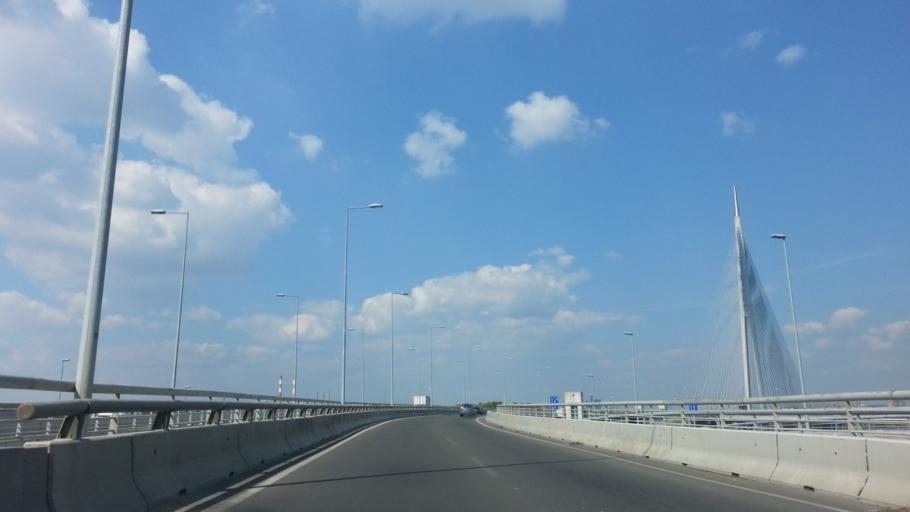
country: RS
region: Central Serbia
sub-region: Belgrade
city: Cukarica
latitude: 44.7896
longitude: 20.4287
